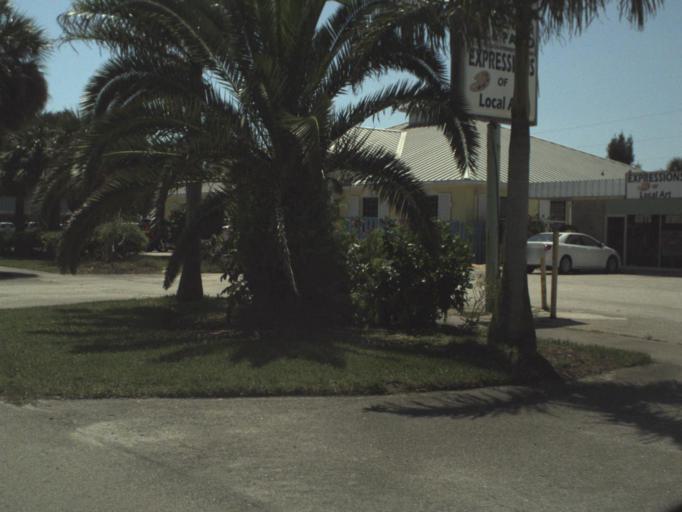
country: US
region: Florida
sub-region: Brevard County
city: Melbourne Beach
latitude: 28.0684
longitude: -80.5593
